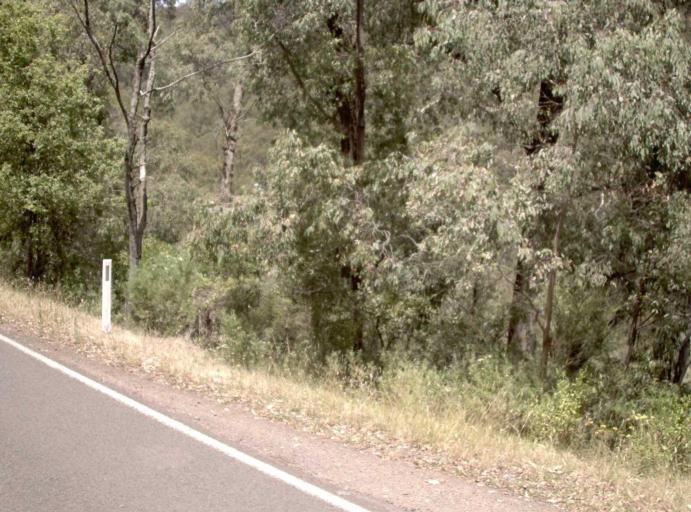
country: AU
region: Victoria
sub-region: Latrobe
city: Traralgon
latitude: -37.9531
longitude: 146.4385
